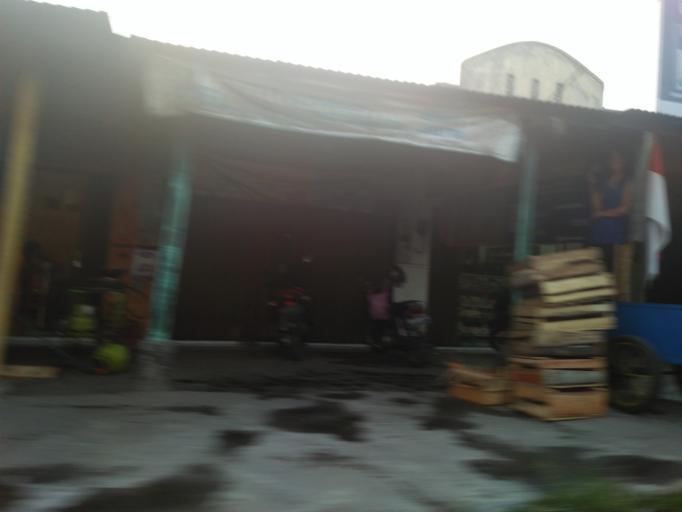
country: ID
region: Daerah Istimewa Yogyakarta
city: Sewon
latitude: -7.8489
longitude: 110.4103
